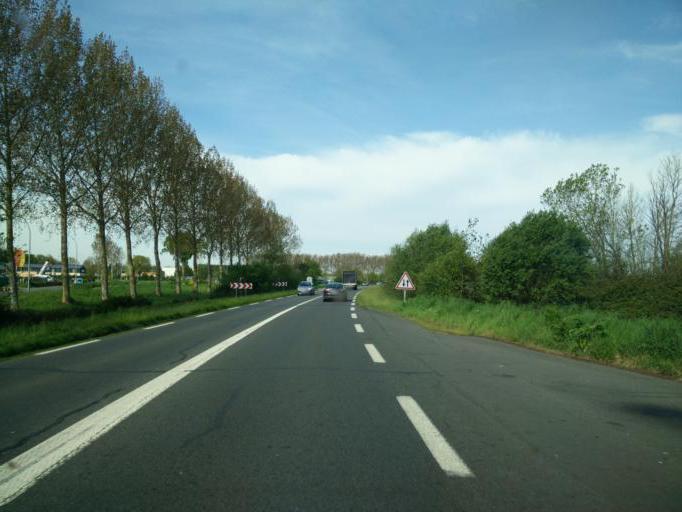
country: FR
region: Lower Normandy
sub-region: Departement de la Manche
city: Pontorson
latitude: 48.5607
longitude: -1.4883
